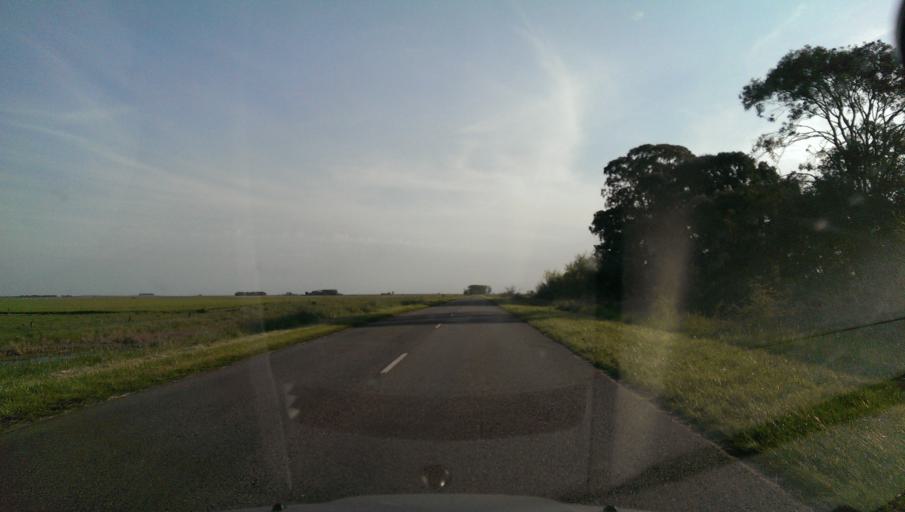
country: AR
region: Buenos Aires
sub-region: Partido de General La Madrid
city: General La Madrid
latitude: -37.5492
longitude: -61.2691
